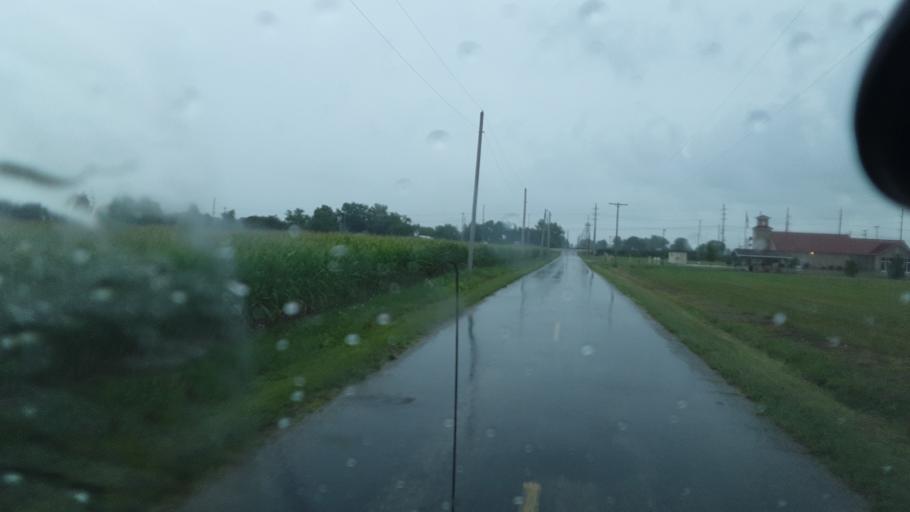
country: US
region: Ohio
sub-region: Williams County
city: Montpelier
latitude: 41.6007
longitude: -84.5596
